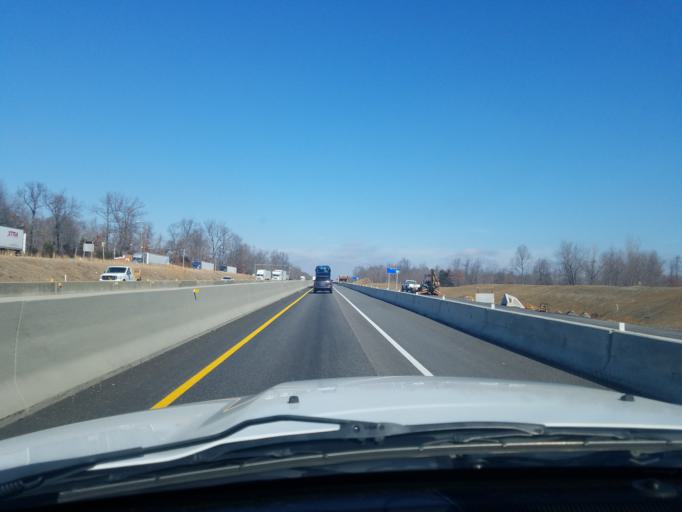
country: US
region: Kentucky
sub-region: Hardin County
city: Elizabethtown
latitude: 37.6524
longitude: -85.8565
